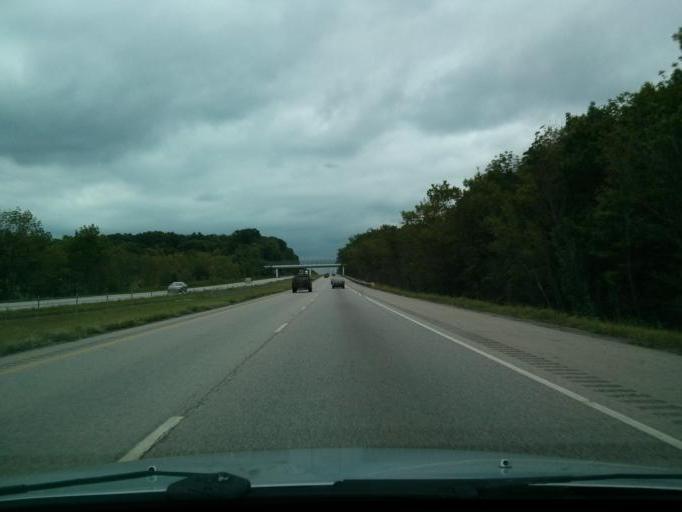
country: US
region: Ohio
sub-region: Mahoning County
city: Craig Beach
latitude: 41.1060
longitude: -81.0935
